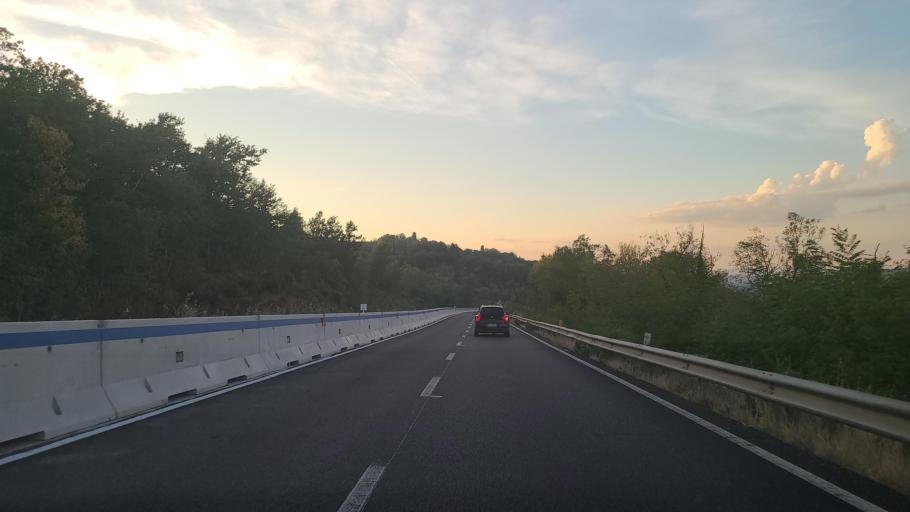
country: IT
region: Tuscany
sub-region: Province of Florence
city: Sambuca
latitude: 43.5693
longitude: 11.2099
